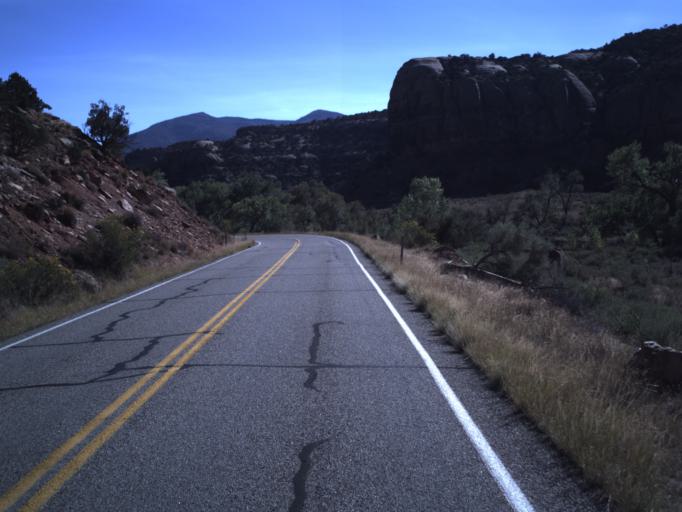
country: US
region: Utah
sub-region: San Juan County
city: Monticello
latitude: 38.0289
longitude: -109.5412
